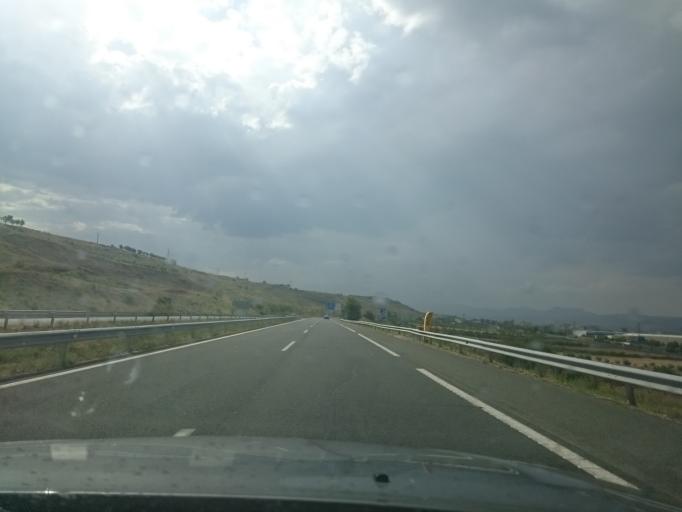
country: ES
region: La Rioja
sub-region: Provincia de La Rioja
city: Agoncillo
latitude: 42.4310
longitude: -2.2821
